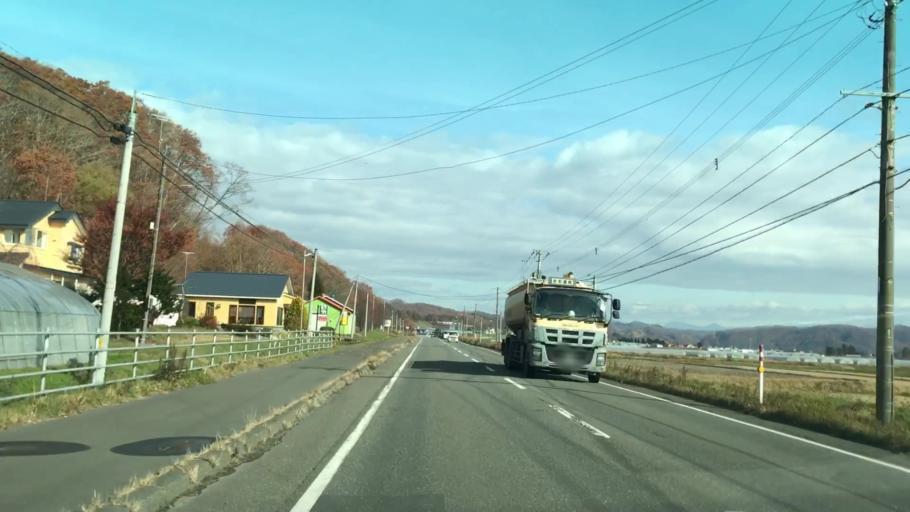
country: JP
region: Hokkaido
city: Shizunai-furukawacho
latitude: 42.5667
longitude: 142.0935
